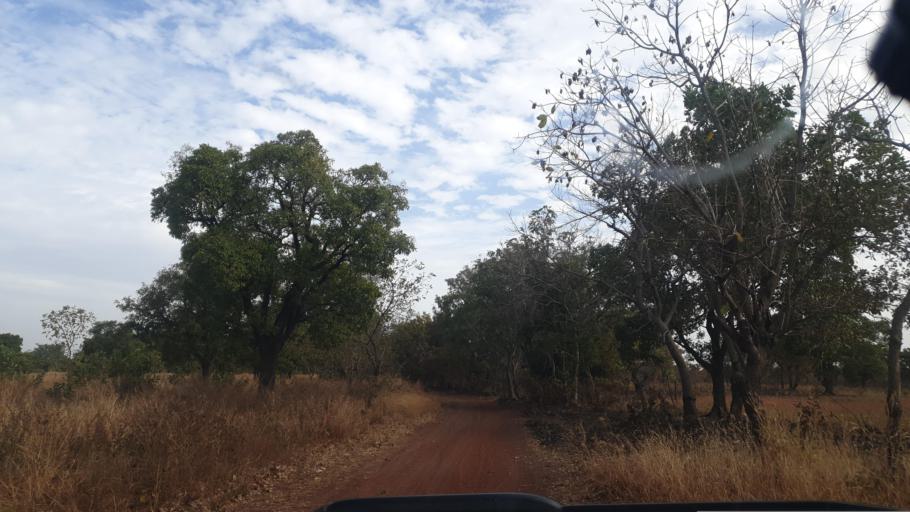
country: ML
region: Sikasso
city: Yanfolila
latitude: 11.3914
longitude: -8.0220
